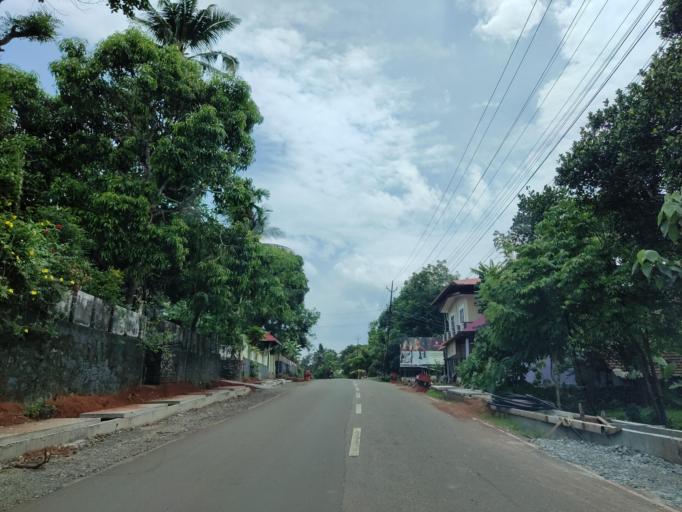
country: IN
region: Kerala
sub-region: Alappuzha
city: Mavelikara
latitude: 9.2302
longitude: 76.6082
